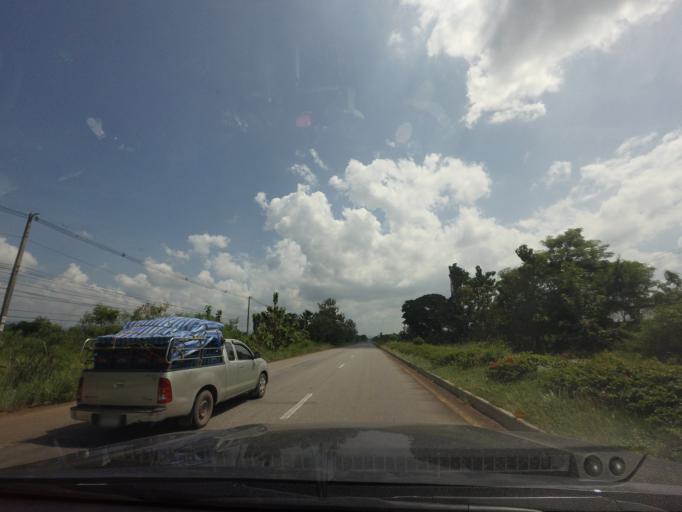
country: TH
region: Phetchabun
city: Phetchabun
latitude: 16.2430
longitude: 101.0749
